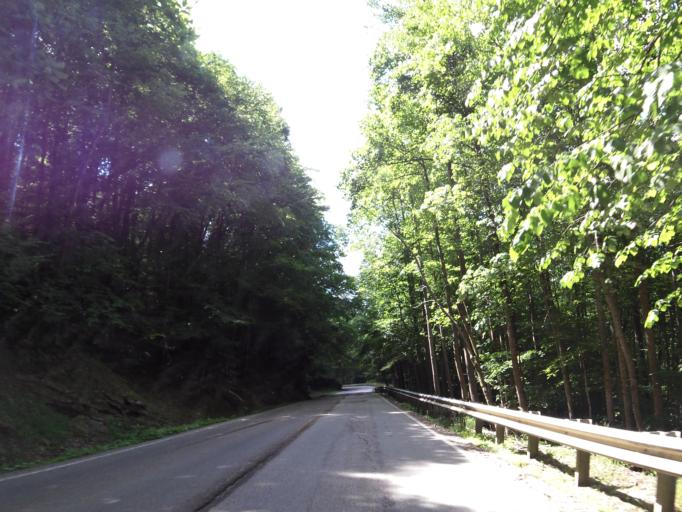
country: US
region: Virginia
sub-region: Lee County
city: Jonesville
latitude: 36.7608
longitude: -83.1370
